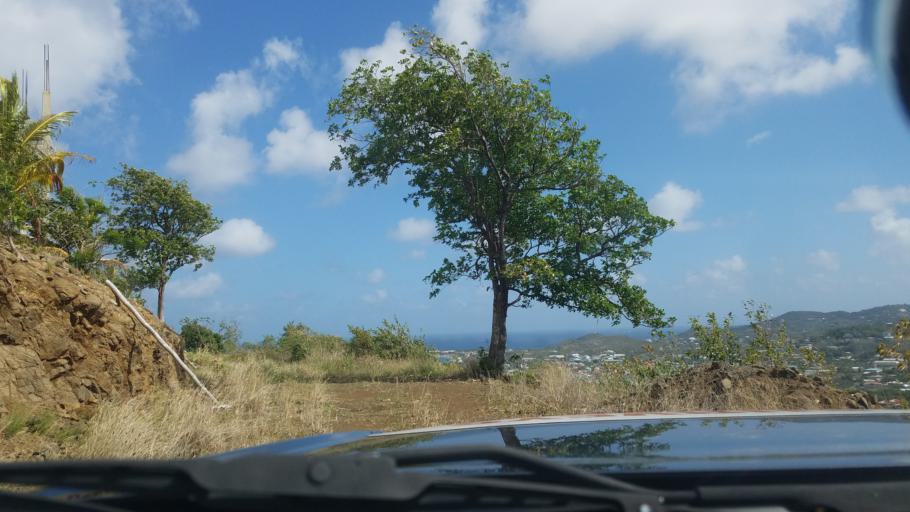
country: LC
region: Gros-Islet
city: Gros Islet
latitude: 14.0642
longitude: -60.9479
